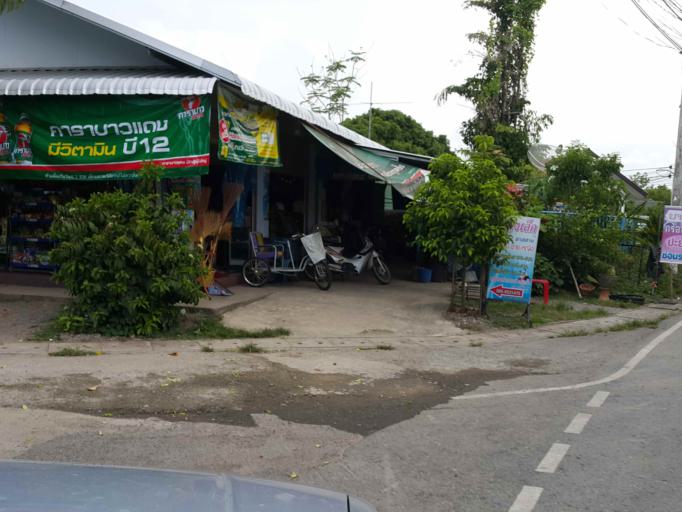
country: TH
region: Chiang Mai
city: Saraphi
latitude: 18.6892
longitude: 99.0280
